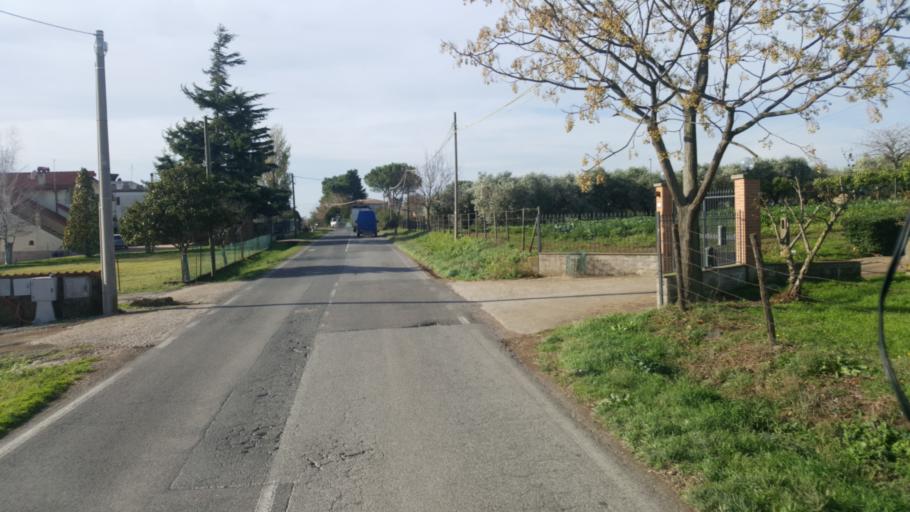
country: IT
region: Latium
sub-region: Provincia di Latina
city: Casalazzara
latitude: 41.6370
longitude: 12.6097
